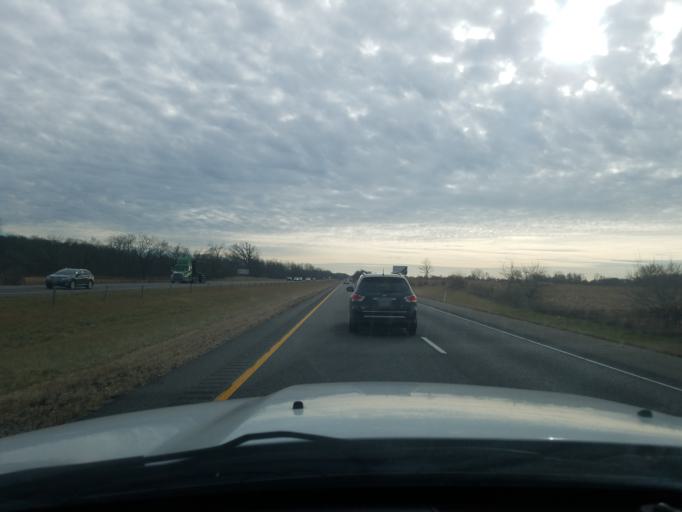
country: US
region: Indiana
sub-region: Delaware County
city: Yorktown
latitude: 40.2536
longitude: -85.5576
